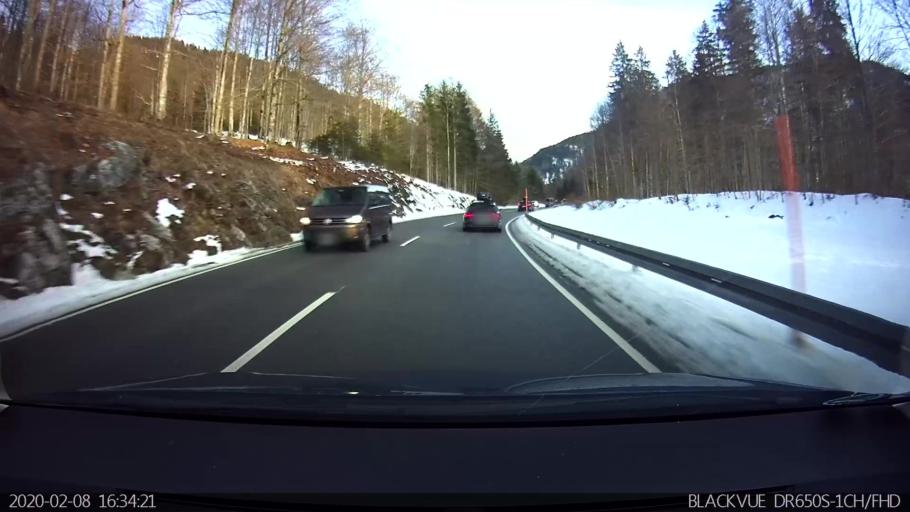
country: DE
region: Bavaria
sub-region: Upper Bavaria
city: Lenggries
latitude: 47.5849
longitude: 11.6018
